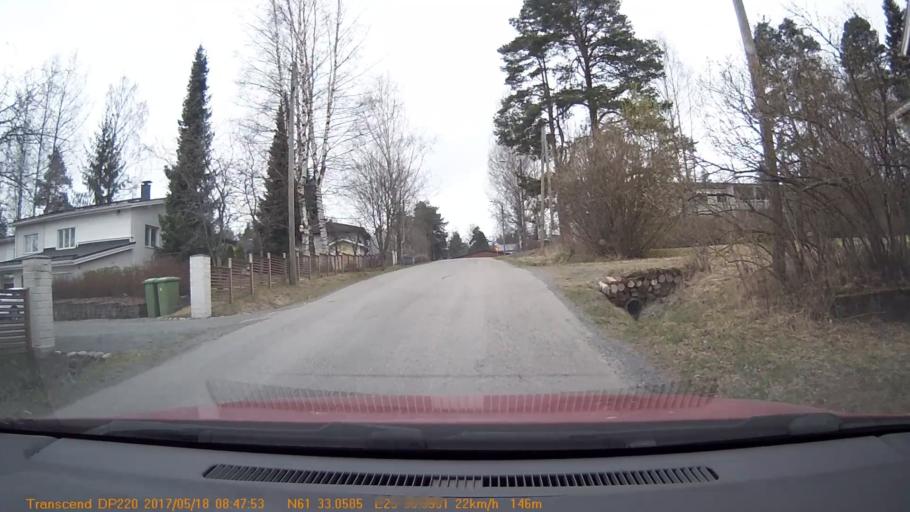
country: FI
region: Pirkanmaa
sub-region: Tampere
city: Yloejaervi
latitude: 61.5511
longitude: 23.5851
